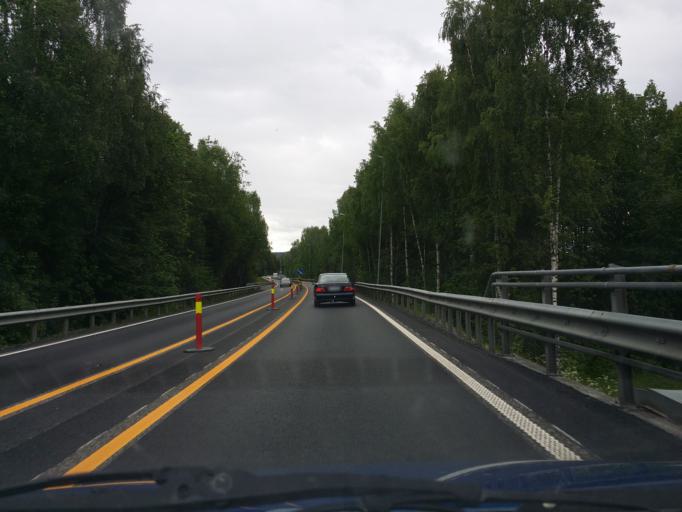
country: NO
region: Hedmark
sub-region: Ringsaker
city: Moelv
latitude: 60.9666
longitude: 10.6058
